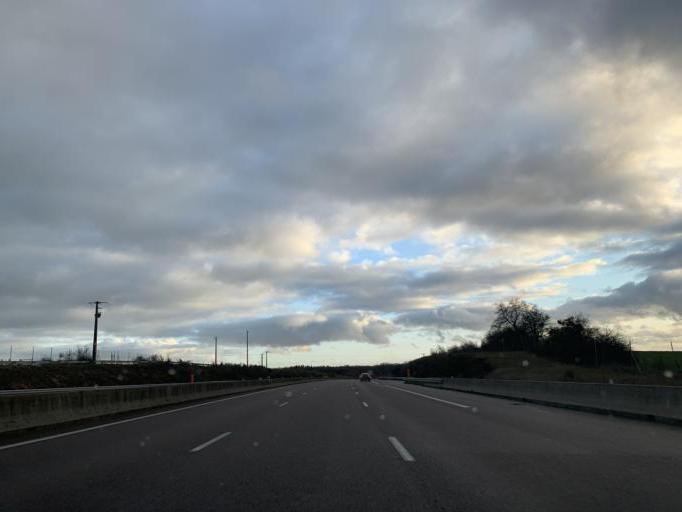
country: FR
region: Bourgogne
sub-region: Departement de la Cote-d'Or
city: Selongey
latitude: 47.7518
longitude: 5.1922
